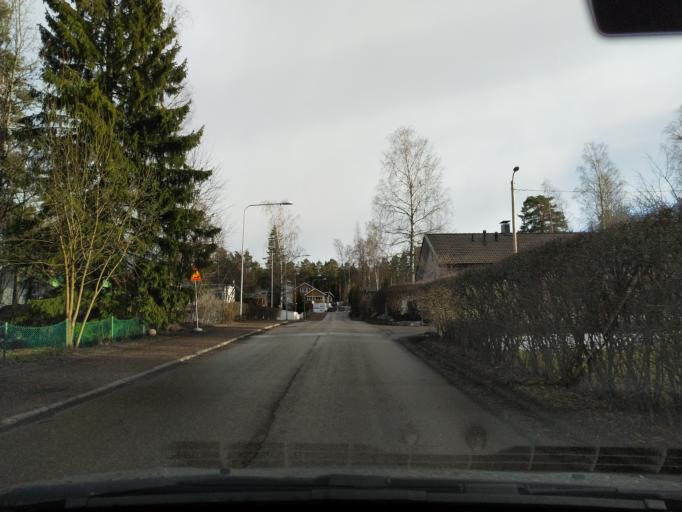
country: FI
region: Uusimaa
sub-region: Helsinki
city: Vantaa
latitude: 60.2818
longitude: 25.0679
